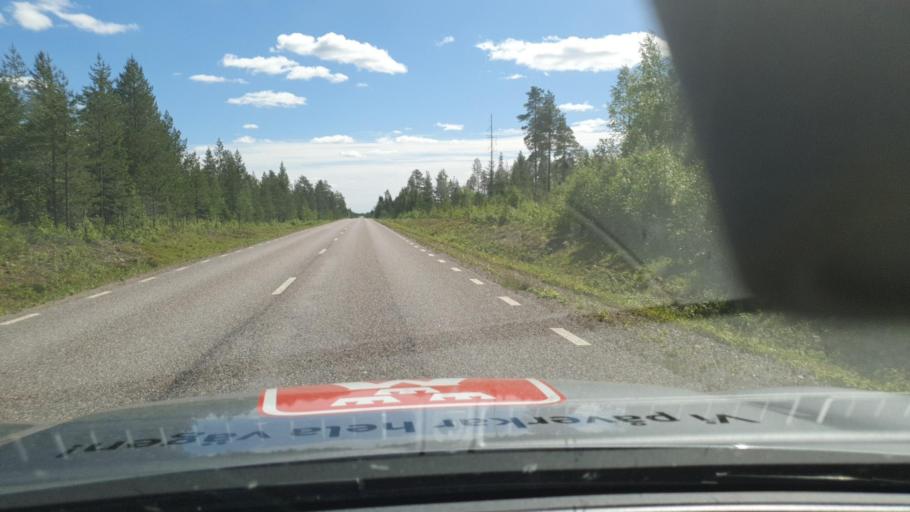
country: SE
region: Norrbotten
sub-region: Pajala Kommun
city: Pajala
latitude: 67.1522
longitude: 23.5574
